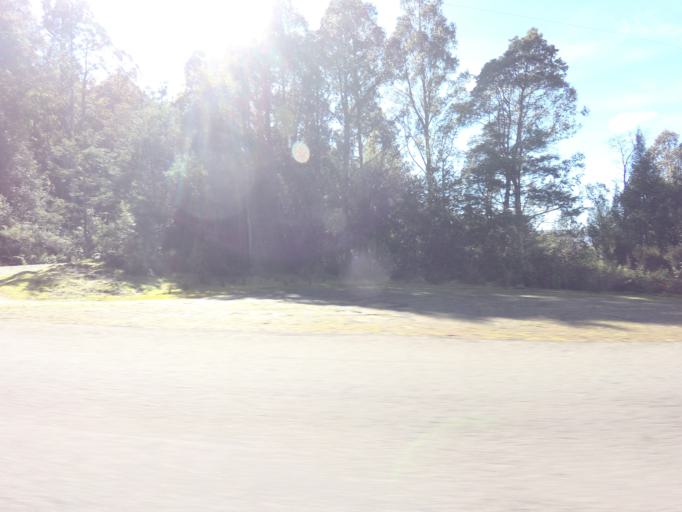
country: AU
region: Tasmania
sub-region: Derwent Valley
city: New Norfolk
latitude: -42.7446
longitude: 146.5007
